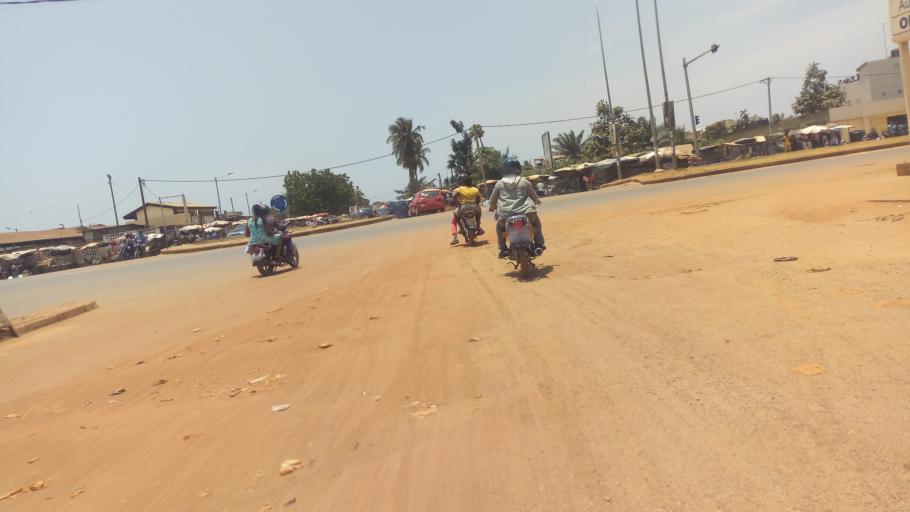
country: TG
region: Maritime
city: Lome
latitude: 6.2306
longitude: 1.1953
